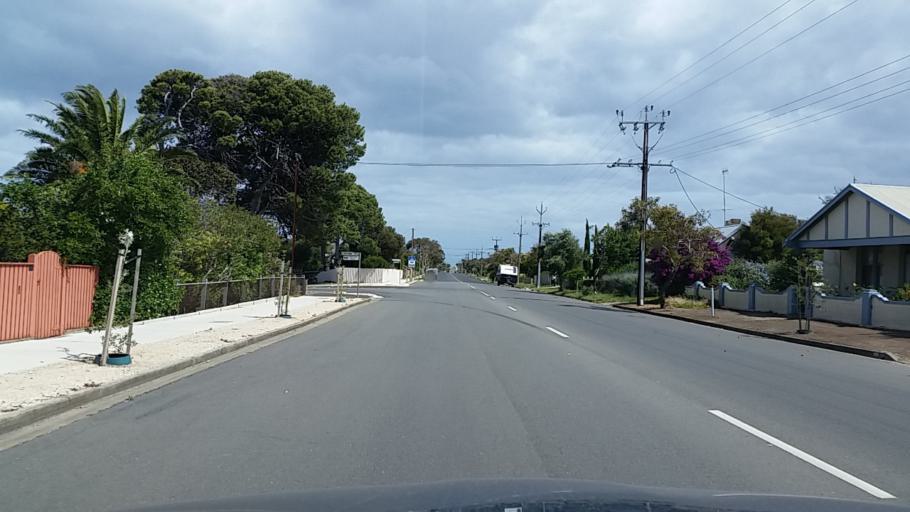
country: AU
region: South Australia
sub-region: Alexandrina
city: Port Elliot
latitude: -35.5253
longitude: 138.6757
